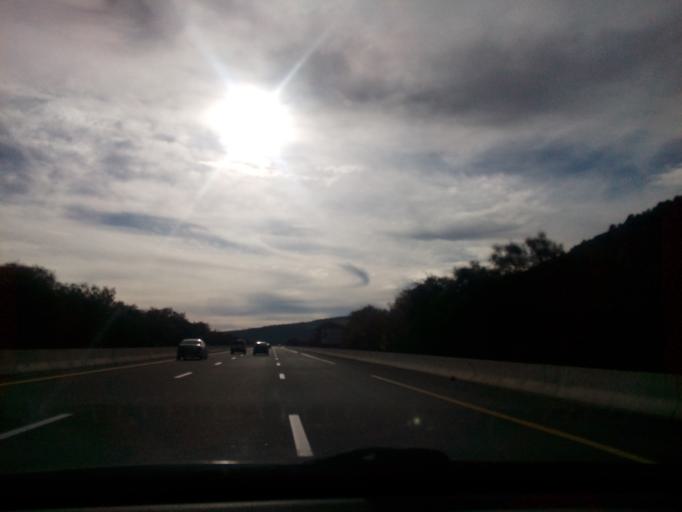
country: DZ
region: Sidi Bel Abbes
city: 'Ain el Berd
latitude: 35.3982
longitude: -0.4905
